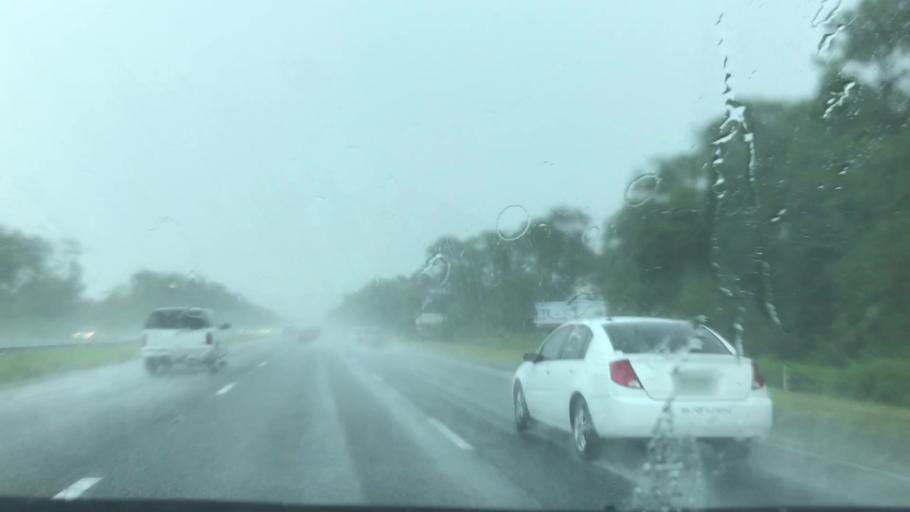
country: US
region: Florida
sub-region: Volusia County
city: Ormond-by-the-Sea
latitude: 29.3827
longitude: -81.1462
